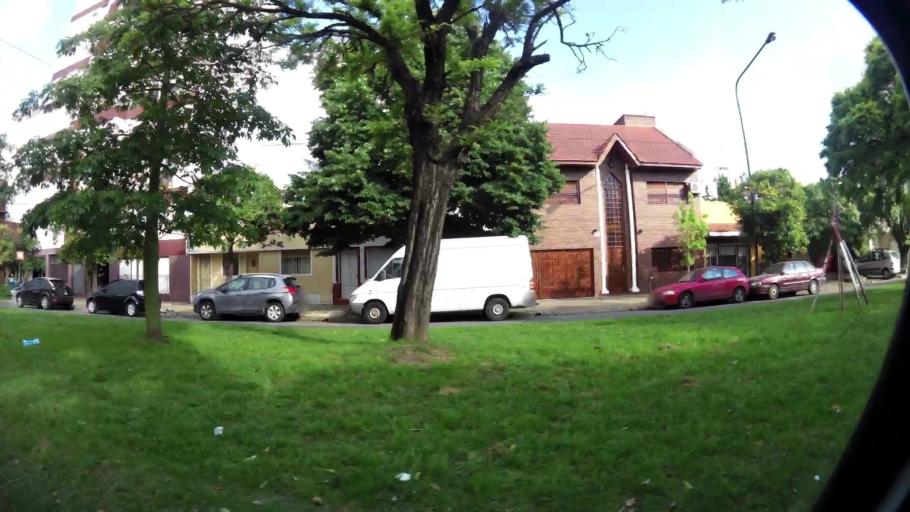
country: AR
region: Buenos Aires
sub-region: Partido de La Plata
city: La Plata
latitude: -34.9031
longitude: -57.9594
